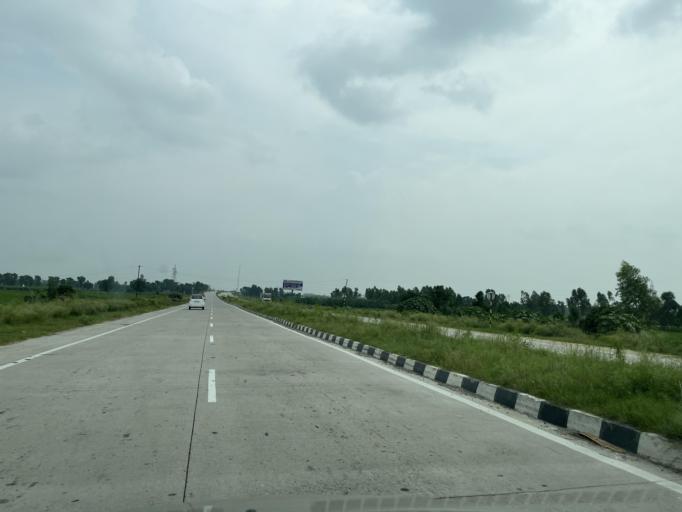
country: IN
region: Uttarakhand
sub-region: Udham Singh Nagar
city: Kashipur
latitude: 29.1962
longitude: 78.9358
